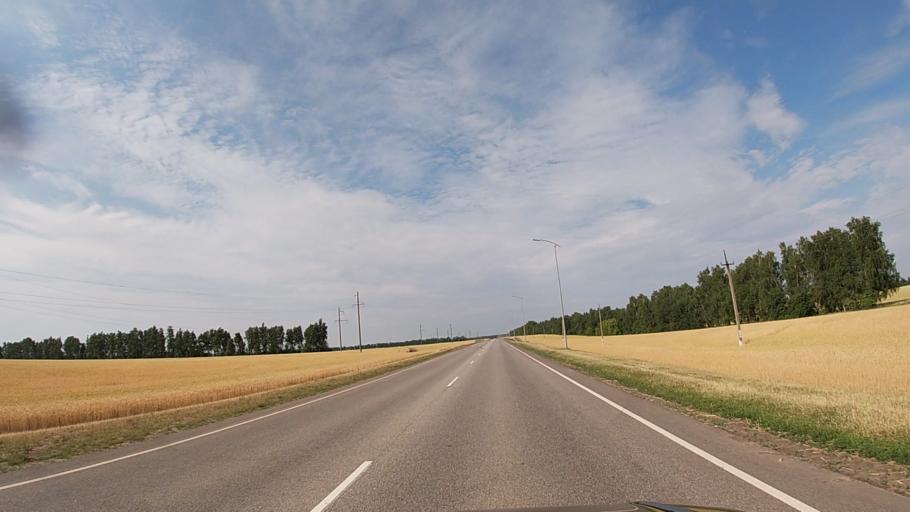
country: RU
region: Belgorod
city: Proletarskiy
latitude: 50.8229
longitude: 35.7583
